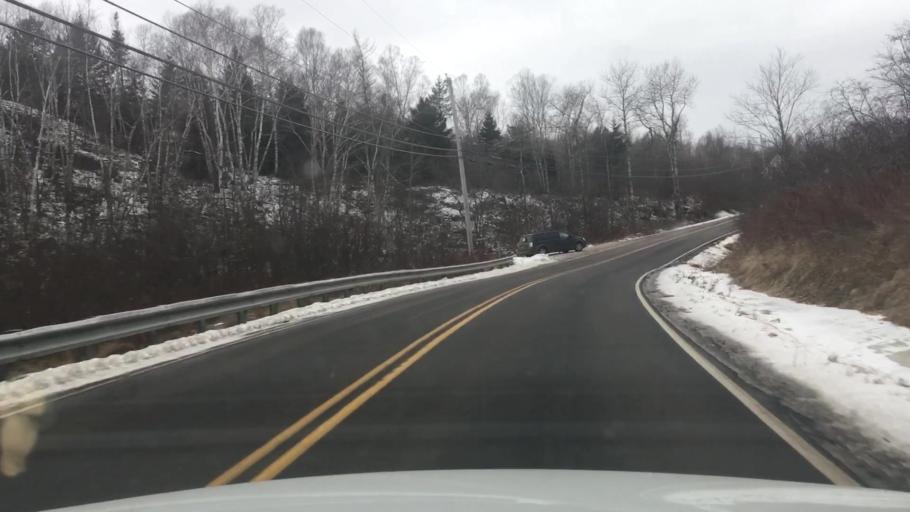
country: US
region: Maine
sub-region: Washington County
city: East Machias
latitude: 44.7250
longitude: -67.3862
